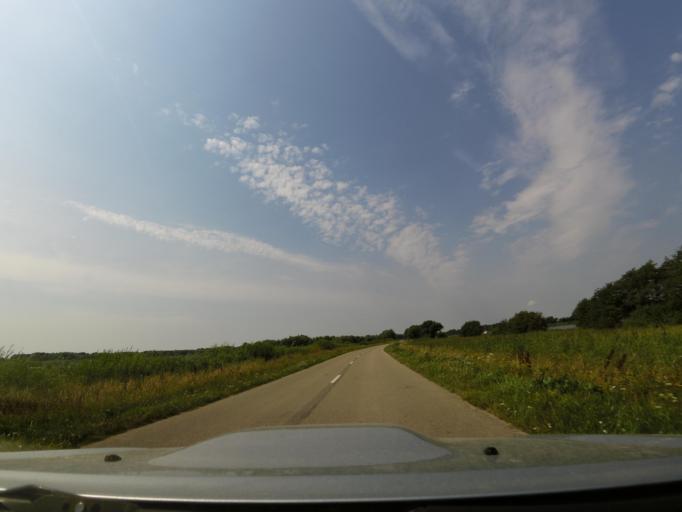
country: LT
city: Rusne
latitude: 55.3432
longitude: 21.3409
